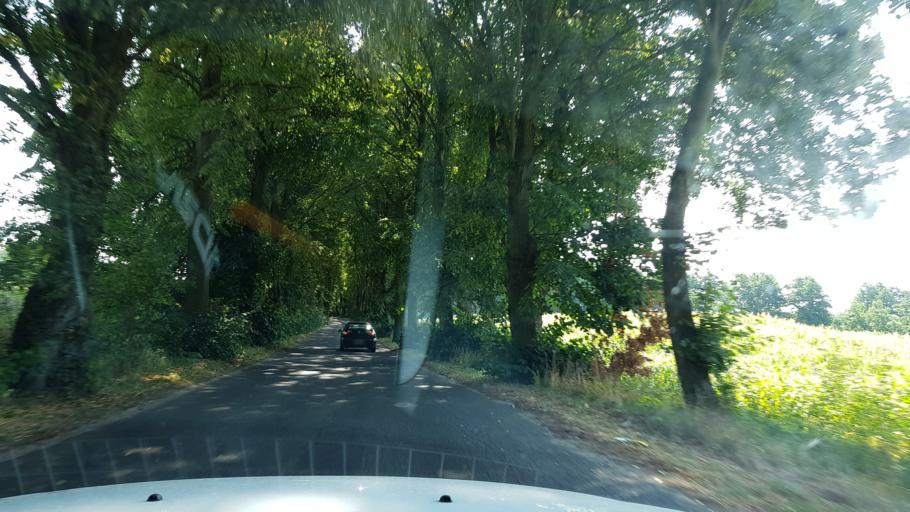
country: PL
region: West Pomeranian Voivodeship
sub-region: Powiat gryfinski
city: Chojna
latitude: 52.9559
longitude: 14.4950
